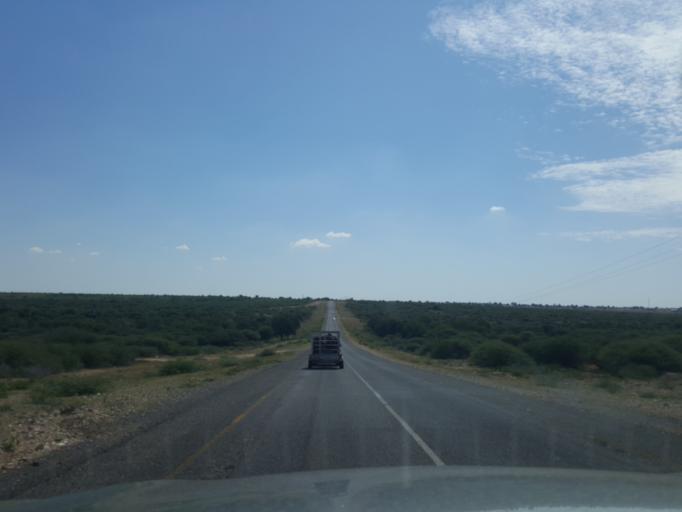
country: BW
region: Kweneng
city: Letlhakeng
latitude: -24.1189
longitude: 25.0608
